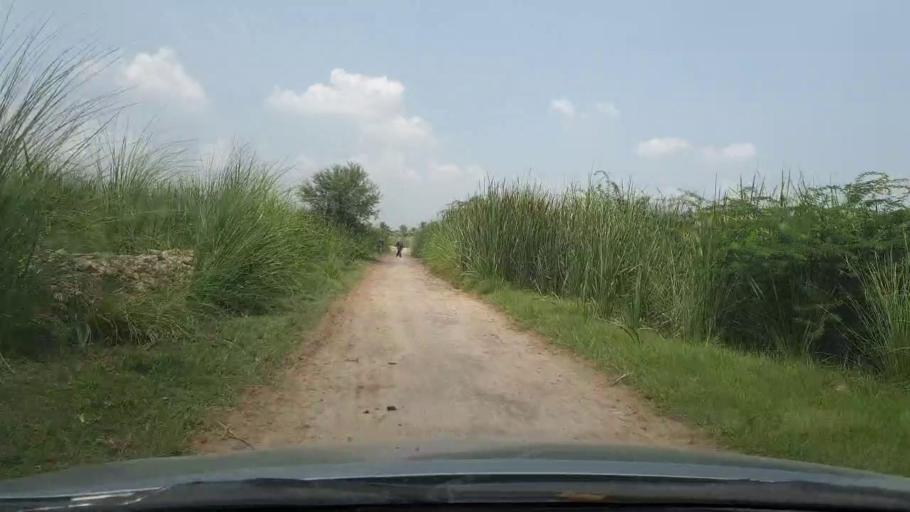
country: PK
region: Sindh
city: Khairpur
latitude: 27.4670
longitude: 68.7382
